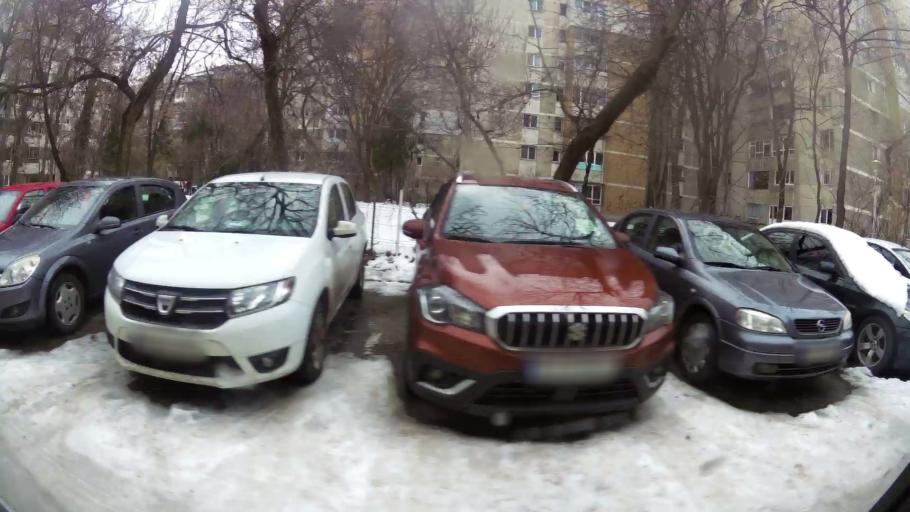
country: RO
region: Ilfov
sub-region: Comuna Chiajna
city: Rosu
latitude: 44.4204
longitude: 26.0418
